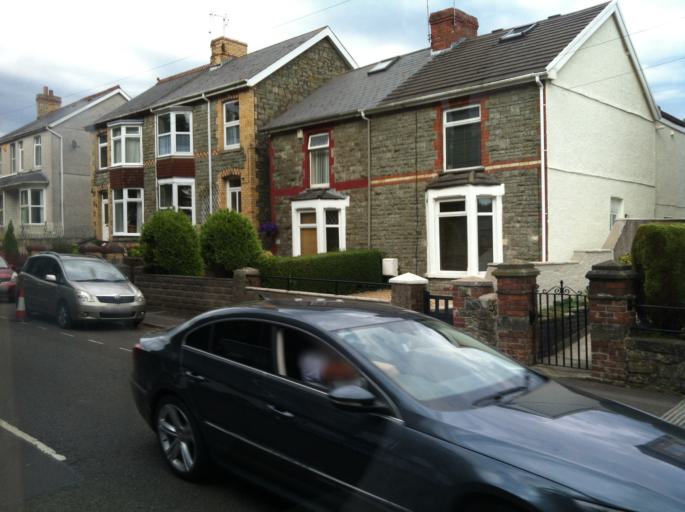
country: GB
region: Wales
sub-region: Bridgend county borough
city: Bridgend
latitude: 51.4974
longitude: -3.5756
